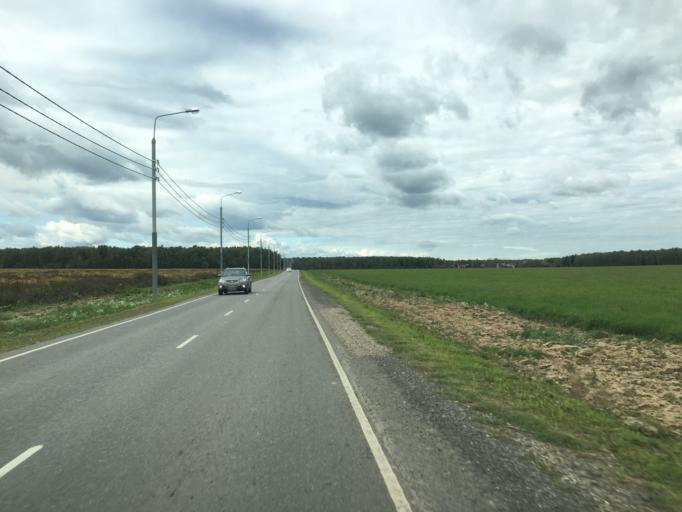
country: RU
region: Moskovskaya
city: Vatutinki
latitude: 55.4924
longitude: 37.3994
